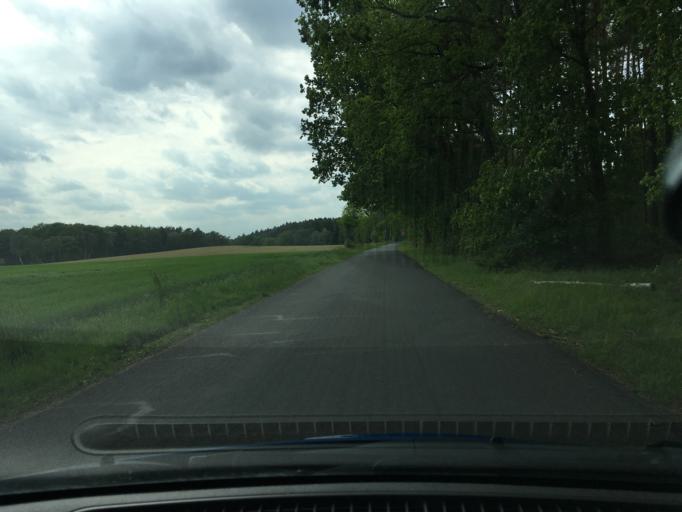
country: DE
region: Lower Saxony
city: Rehlingen
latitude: 53.1026
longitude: 10.2456
